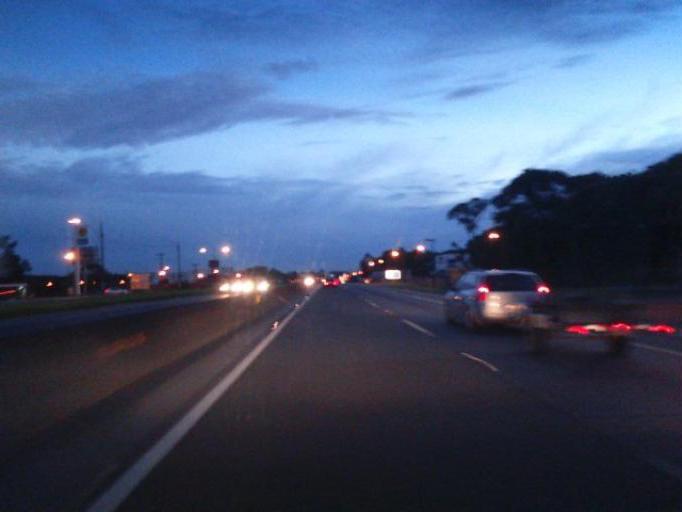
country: BR
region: Santa Catarina
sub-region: Barra Velha
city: Barra Velha
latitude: -26.5293
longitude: -48.7149
